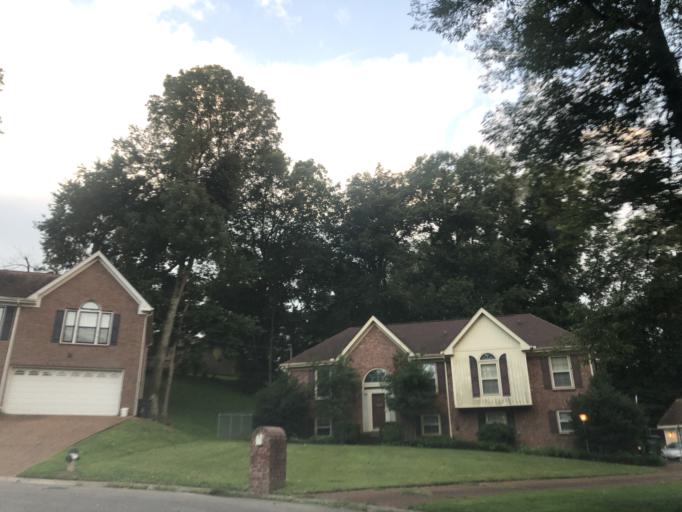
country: US
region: Tennessee
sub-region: Davidson County
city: Lakewood
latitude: 36.1455
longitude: -86.6358
